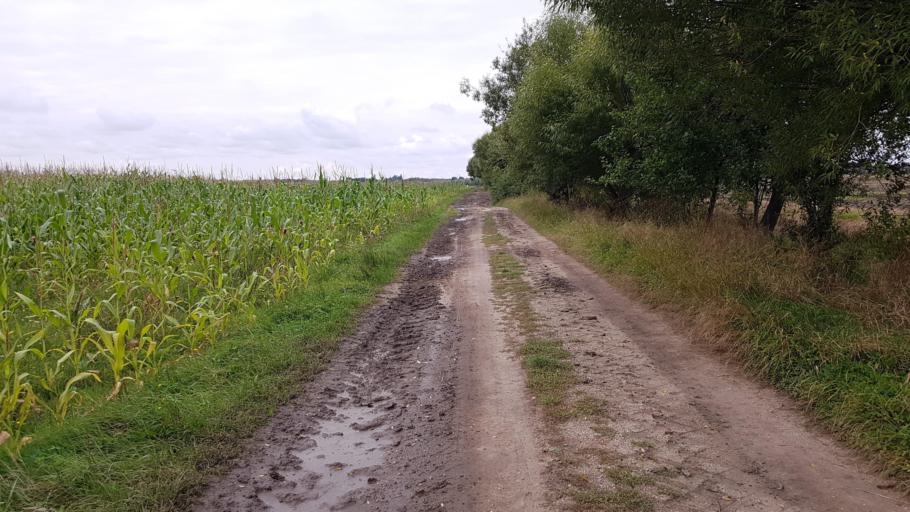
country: DE
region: Brandenburg
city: Doberlug-Kirchhain
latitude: 51.6111
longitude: 13.5819
